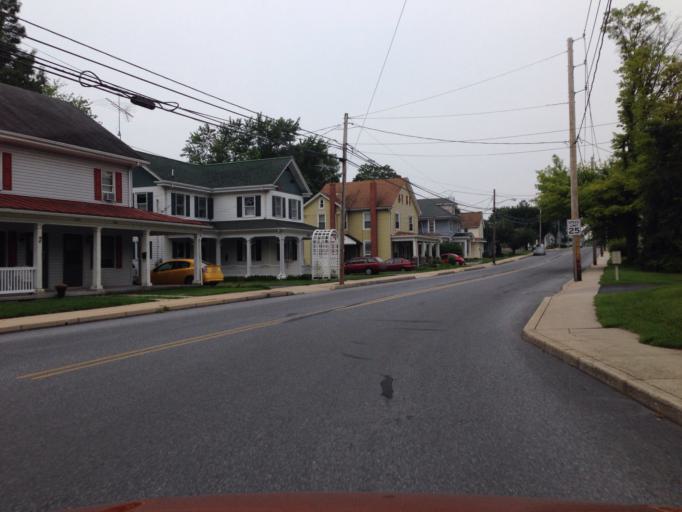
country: US
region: Pennsylvania
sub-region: Lancaster County
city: Akron
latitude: 40.1561
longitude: -76.1958
